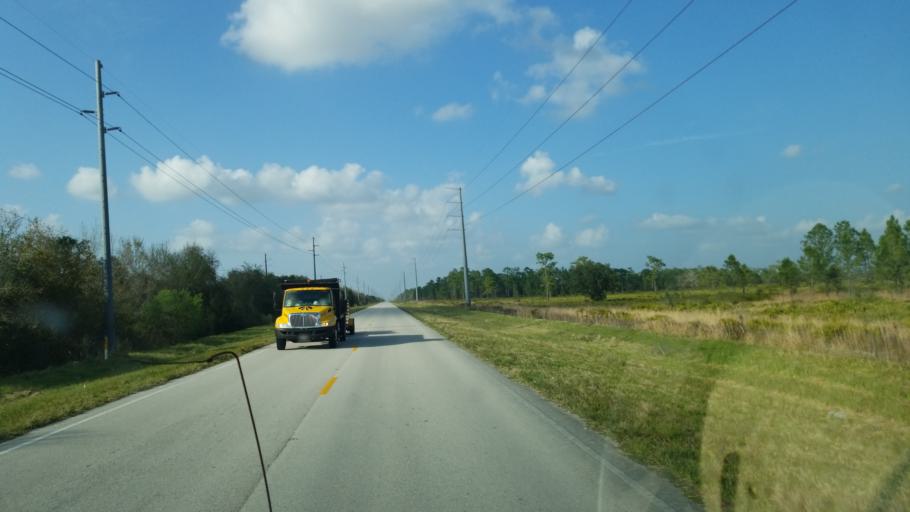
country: US
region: Florida
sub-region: Hardee County
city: Wauchula
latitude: 27.4945
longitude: -81.9216
